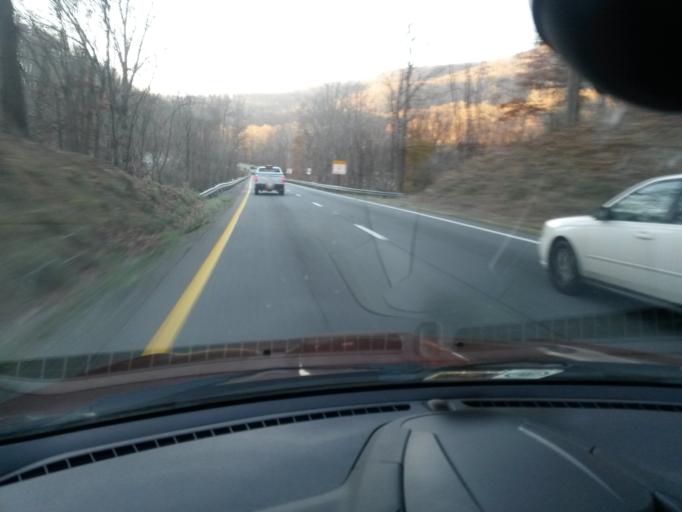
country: US
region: Virginia
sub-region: Roanoke County
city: Narrows
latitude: 37.1377
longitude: -79.9730
